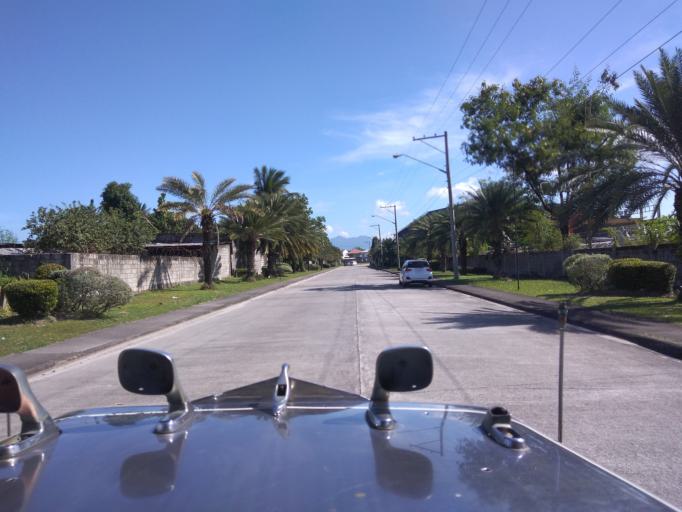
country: PH
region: Central Luzon
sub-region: Province of Pampanga
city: Calibutbut
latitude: 15.1064
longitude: 120.6038
